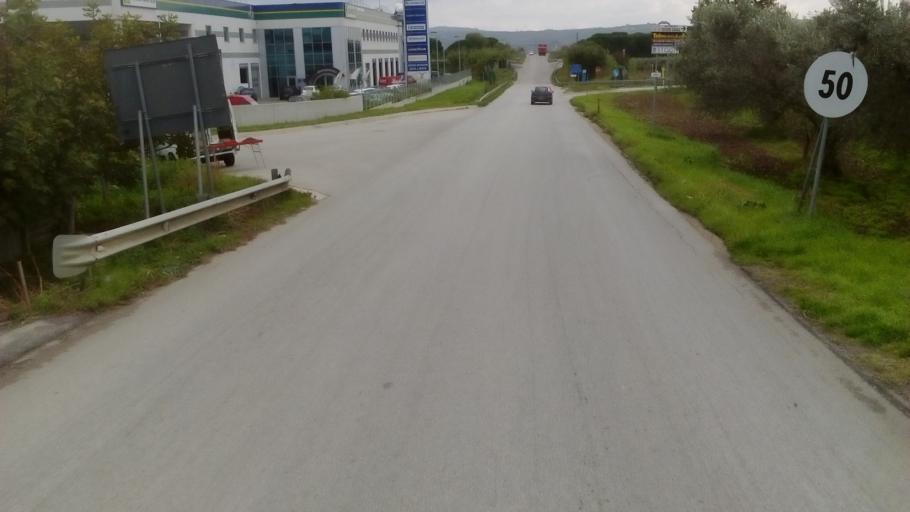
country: IT
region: Abruzzo
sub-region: Provincia di Chieti
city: San Salvo
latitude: 42.0332
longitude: 14.7418
